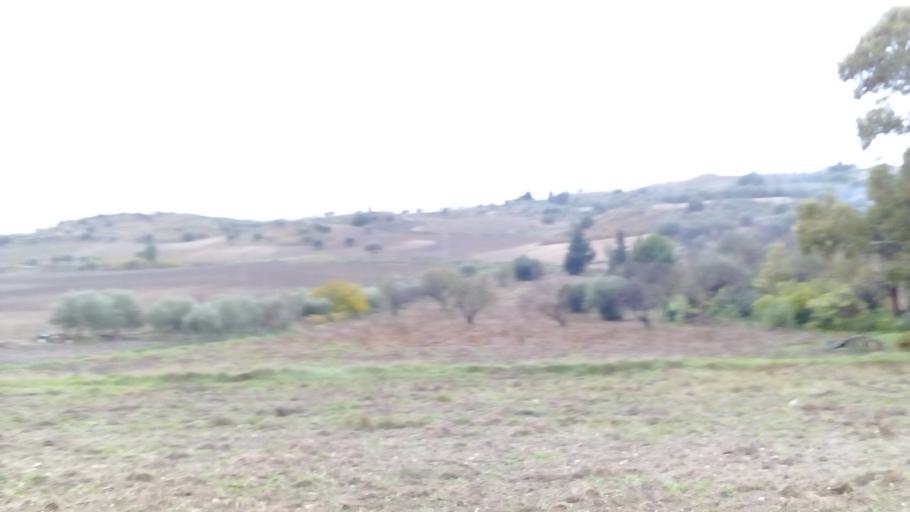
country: IT
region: Sicily
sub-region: Enna
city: Pietraperzia
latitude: 37.4094
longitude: 14.1421
